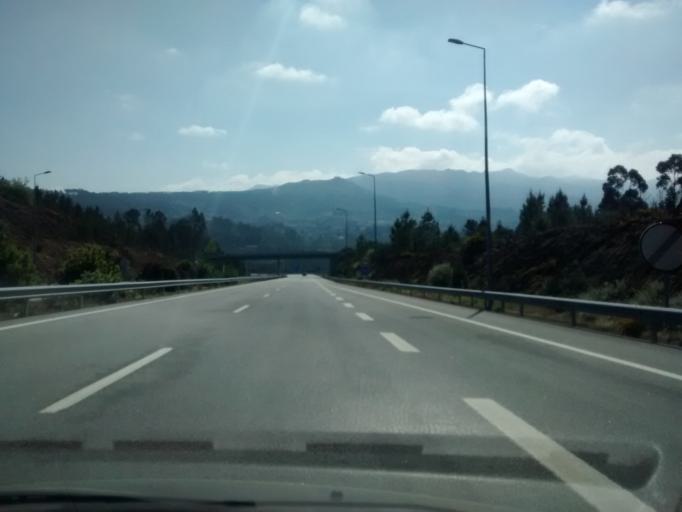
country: PT
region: Braga
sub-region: Cabeceiras de Basto
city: Cabeceiras de Basto
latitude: 41.4730
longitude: -7.9463
